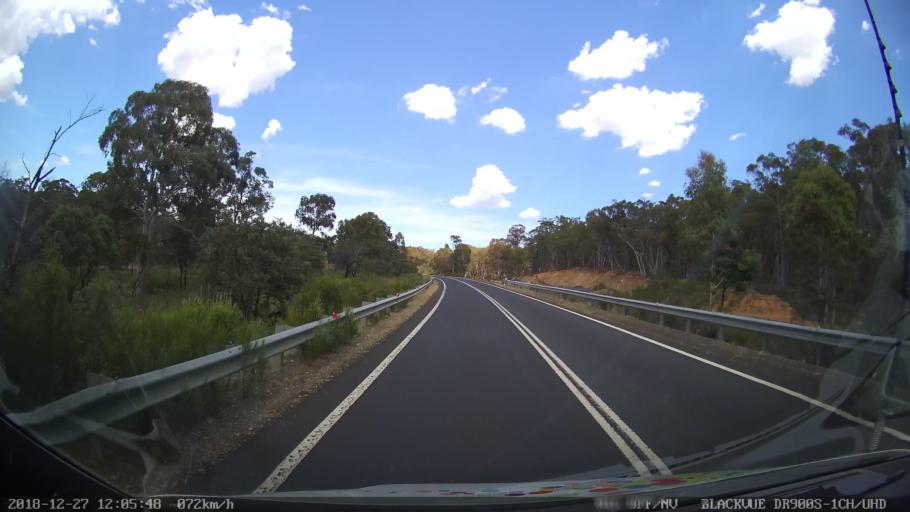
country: AU
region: New South Wales
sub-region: Blayney
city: Blayney
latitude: -33.8039
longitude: 149.3344
